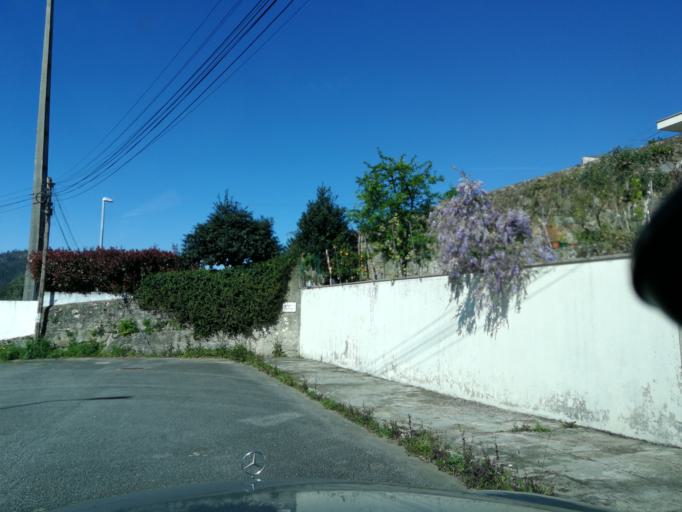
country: PT
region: Braga
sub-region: Braga
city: Braga
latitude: 41.5404
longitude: -8.4462
